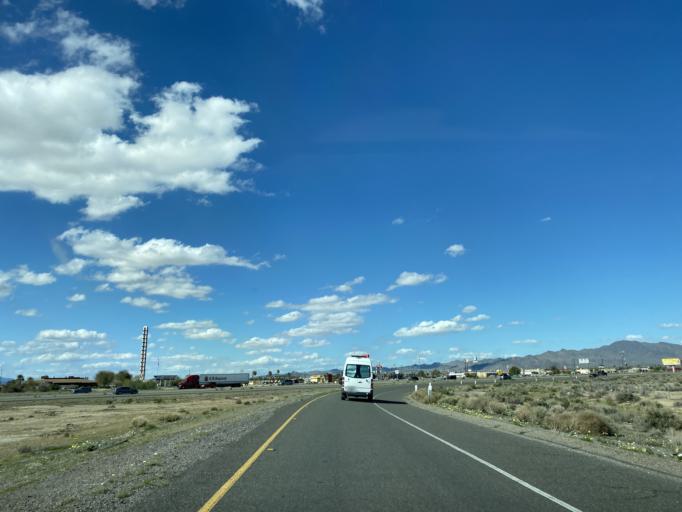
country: US
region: California
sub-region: San Bernardino County
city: Fort Irwin
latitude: 35.2630
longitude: -116.0713
